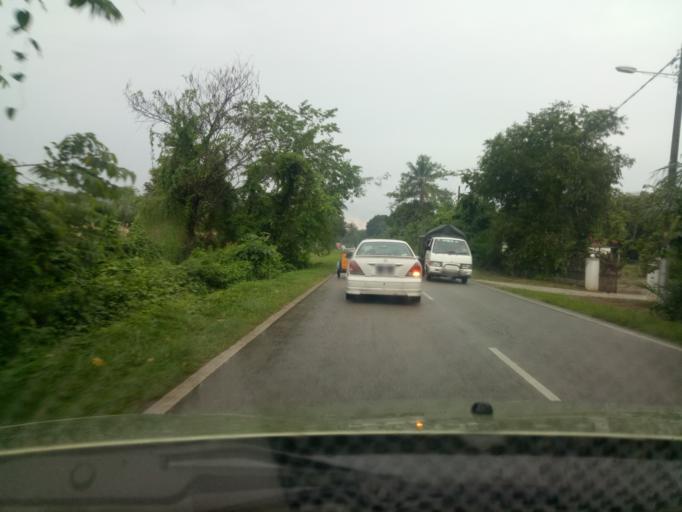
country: MY
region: Penang
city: Tasek Glugor
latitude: 5.5414
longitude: 100.5700
